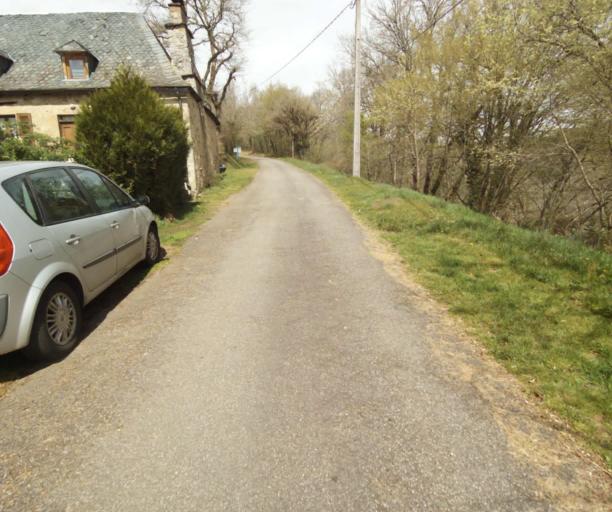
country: FR
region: Limousin
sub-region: Departement de la Correze
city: Argentat
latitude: 45.1754
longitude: 1.8721
